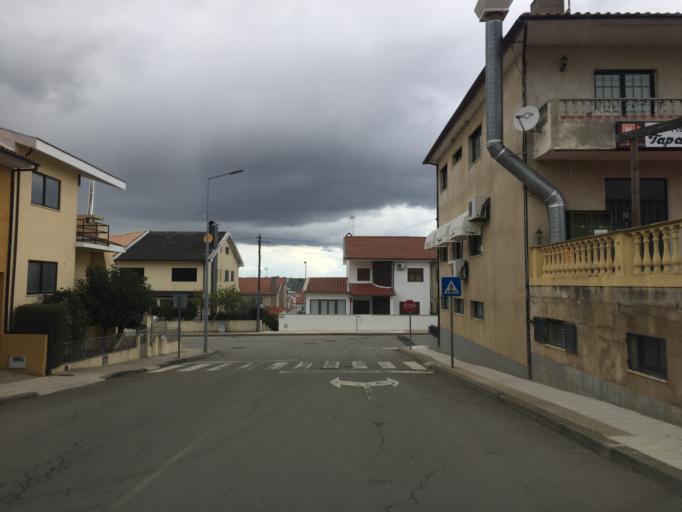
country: PT
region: Braganca
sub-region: Mogadouro
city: Mogadouro
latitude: 41.3433
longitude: -6.7047
